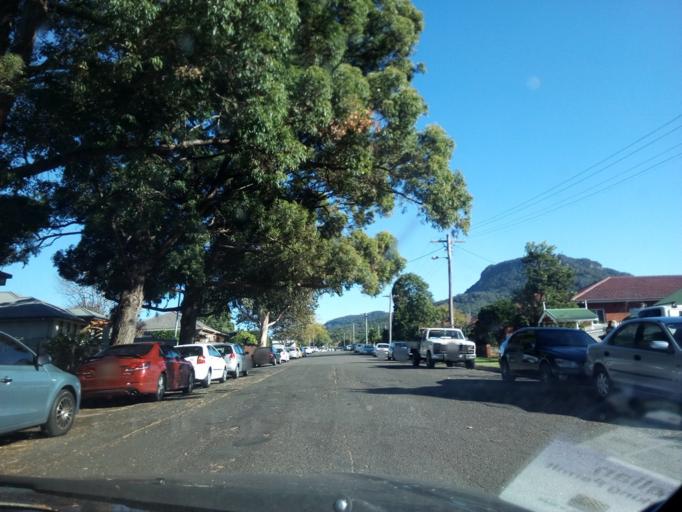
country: AU
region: New South Wales
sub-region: Wollongong
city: Gwynneville
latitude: -34.4140
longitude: 150.8793
